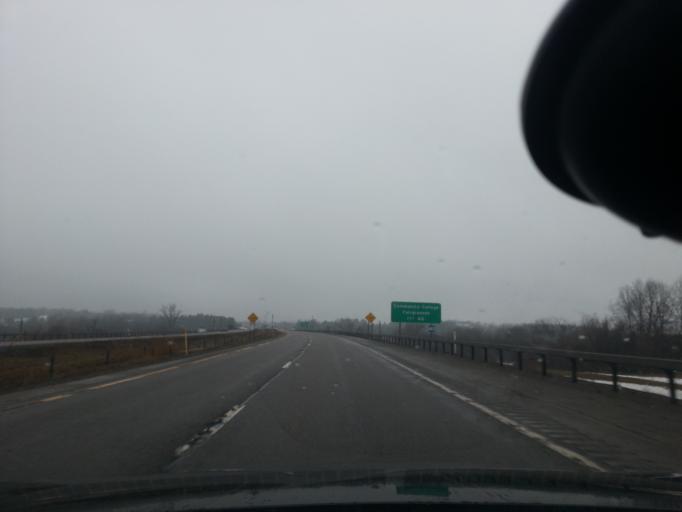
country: US
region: New York
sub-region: Jefferson County
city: Watertown
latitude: 43.9992
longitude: -75.9268
